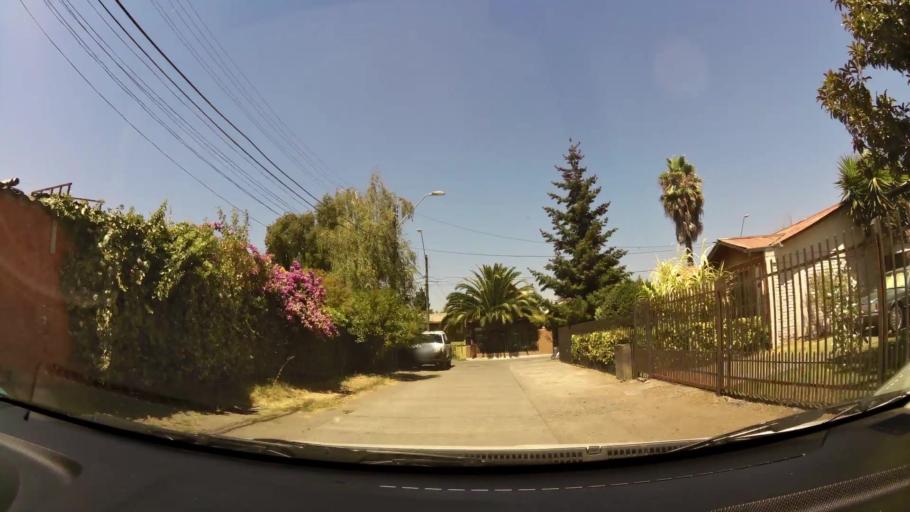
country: CL
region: Maule
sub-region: Provincia de Curico
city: Curico
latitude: -34.9824
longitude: -71.2284
